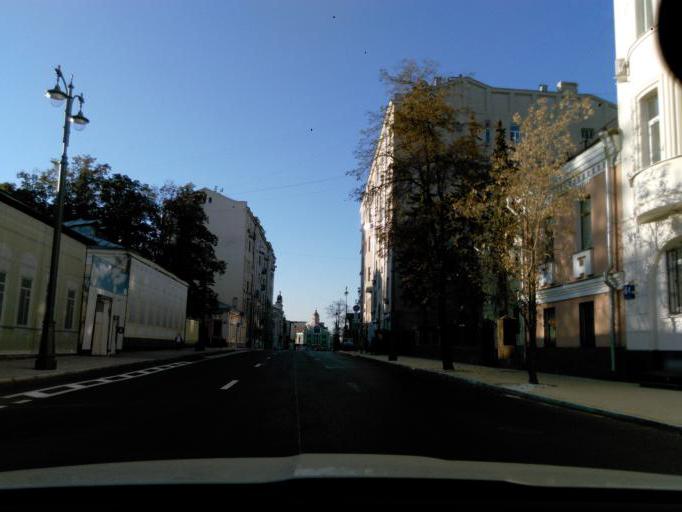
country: RU
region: Moscow
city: Zamoskvorech'ye
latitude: 55.7324
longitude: 37.6242
